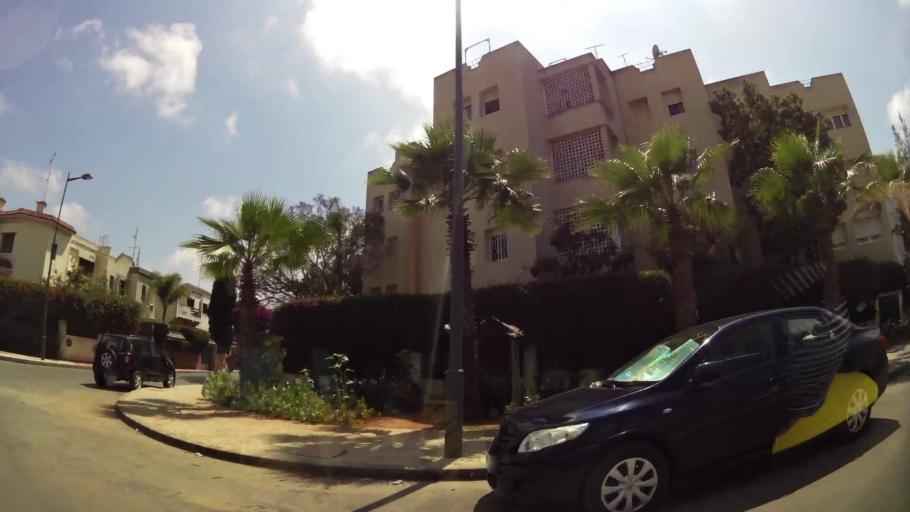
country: MA
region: Rabat-Sale-Zemmour-Zaer
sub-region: Skhirate-Temara
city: Temara
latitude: 33.9567
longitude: -6.8812
